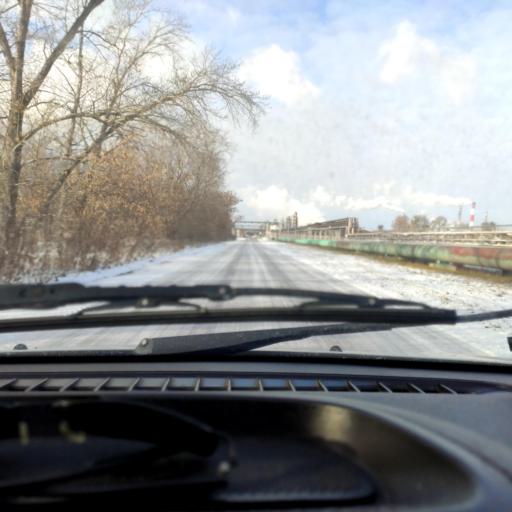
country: RU
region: Samara
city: Tol'yatti
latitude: 53.5349
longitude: 49.4772
